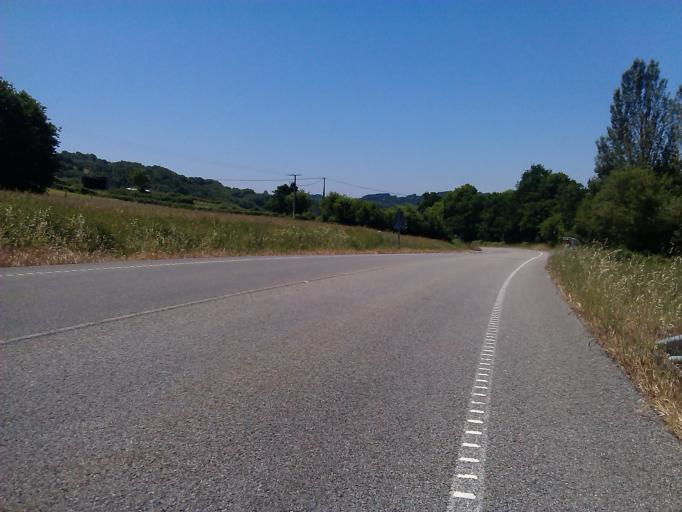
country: ES
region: Galicia
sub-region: Provincia de Lugo
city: Samos
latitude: 42.7382
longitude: -7.3075
